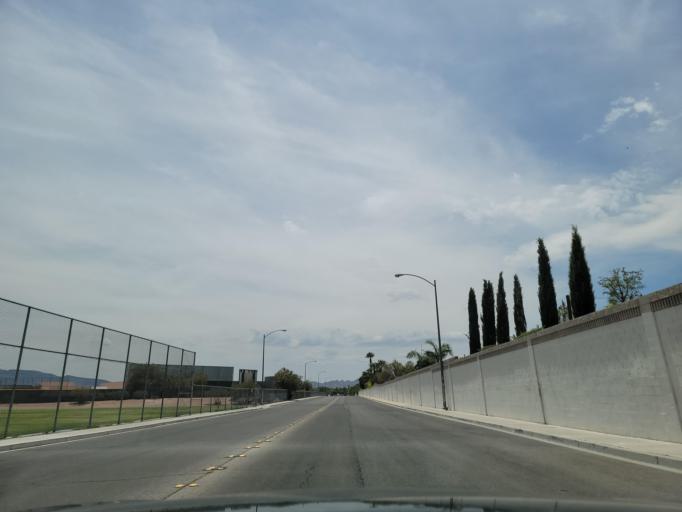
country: US
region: Nevada
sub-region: Clark County
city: Whitney
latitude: 36.0269
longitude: -115.1318
